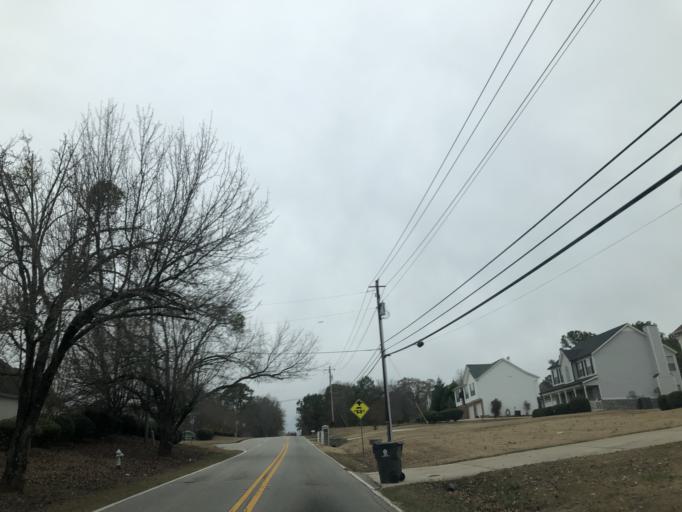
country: US
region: Georgia
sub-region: Henry County
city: Stockbridge
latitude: 33.6054
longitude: -84.2656
